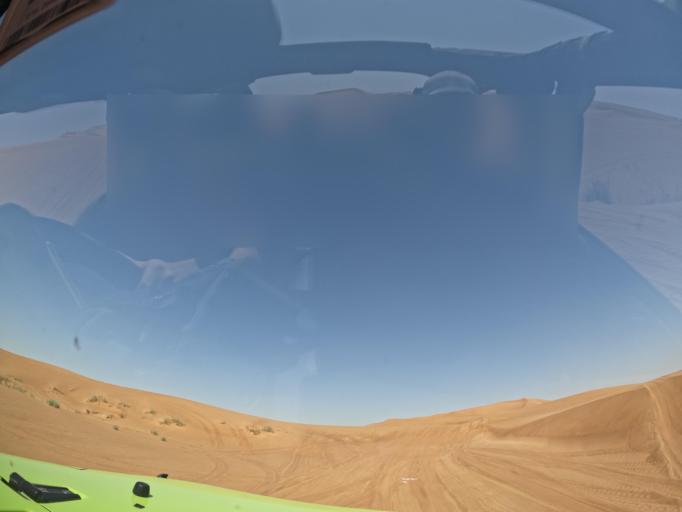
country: AE
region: Ash Shariqah
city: Adh Dhayd
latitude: 24.9691
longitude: 55.7203
